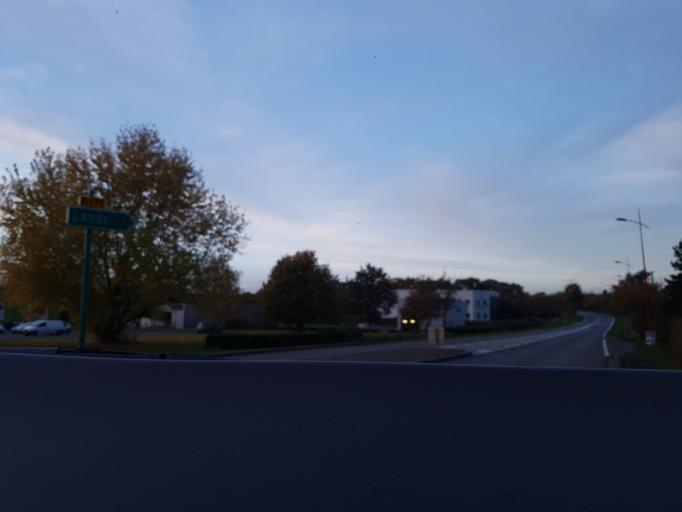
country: FR
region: Pays de la Loire
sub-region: Departement de la Mayenne
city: Cosse-le-Vivien
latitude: 47.9364
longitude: -0.9153
